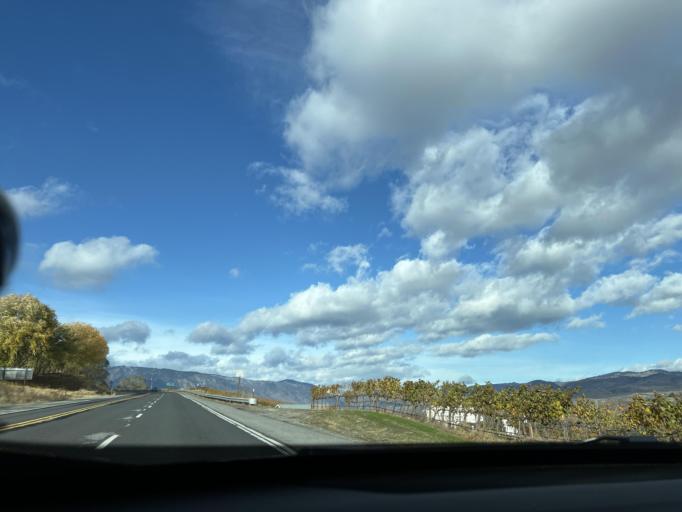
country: US
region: Washington
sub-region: Chelan County
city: Manson
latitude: 47.8400
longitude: -120.0968
